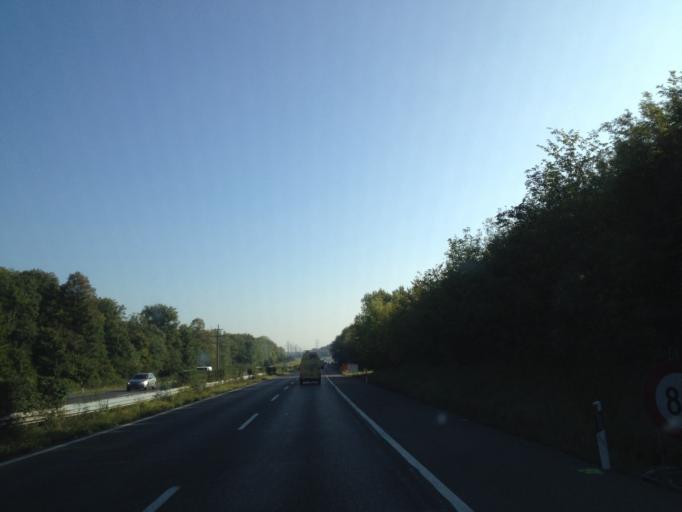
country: CH
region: Vaud
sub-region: Nyon District
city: Prangins
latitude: 46.4150
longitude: 6.2357
